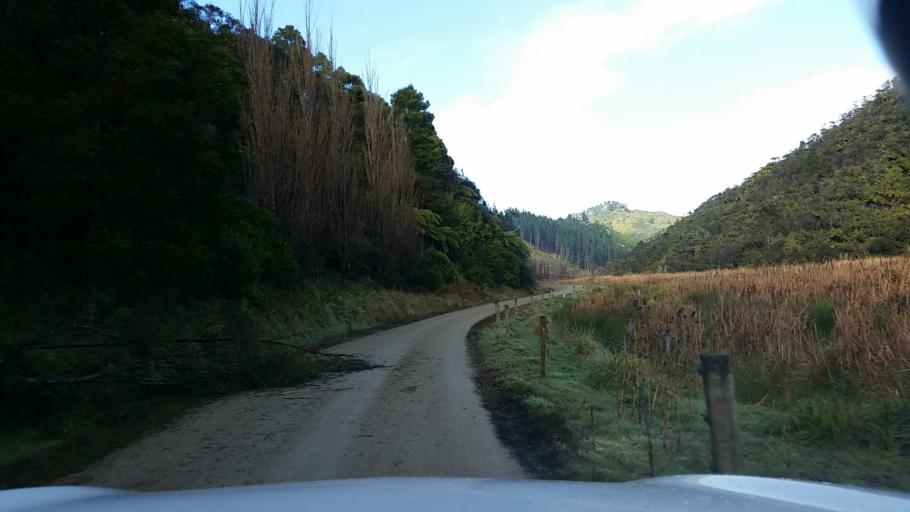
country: NZ
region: Taranaki
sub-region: South Taranaki District
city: Patea
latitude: -39.6803
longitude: 174.7652
